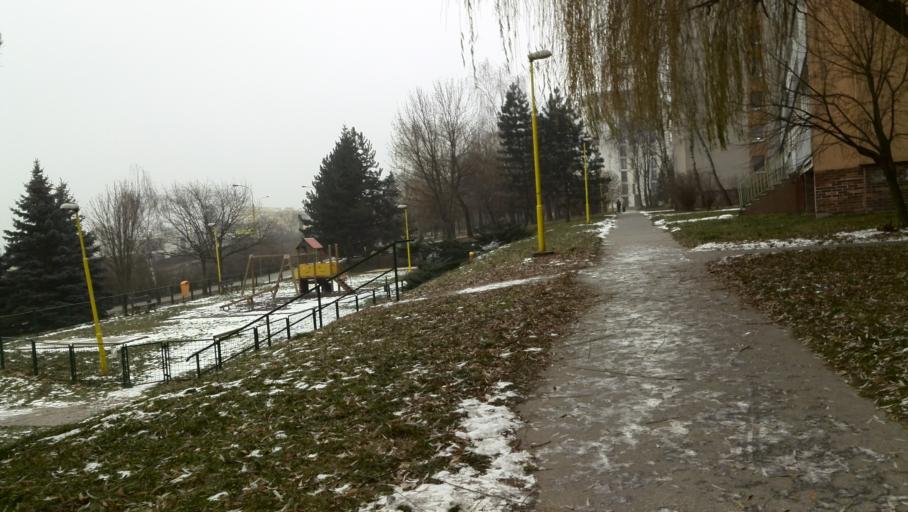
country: SK
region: Kosicky
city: Kosice
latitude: 48.7119
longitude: 21.2451
